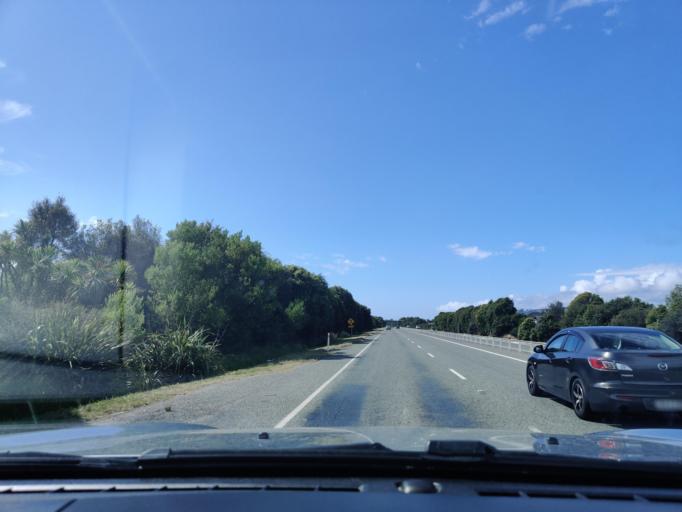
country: NZ
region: Tasman
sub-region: Tasman District
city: Richmond
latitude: -41.3114
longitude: 173.2172
